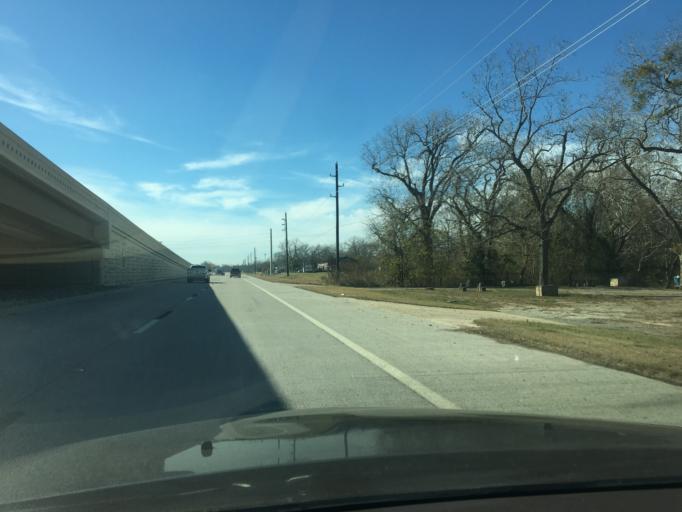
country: US
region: Texas
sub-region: Fort Bend County
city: Richmond
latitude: 29.5934
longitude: -95.7435
